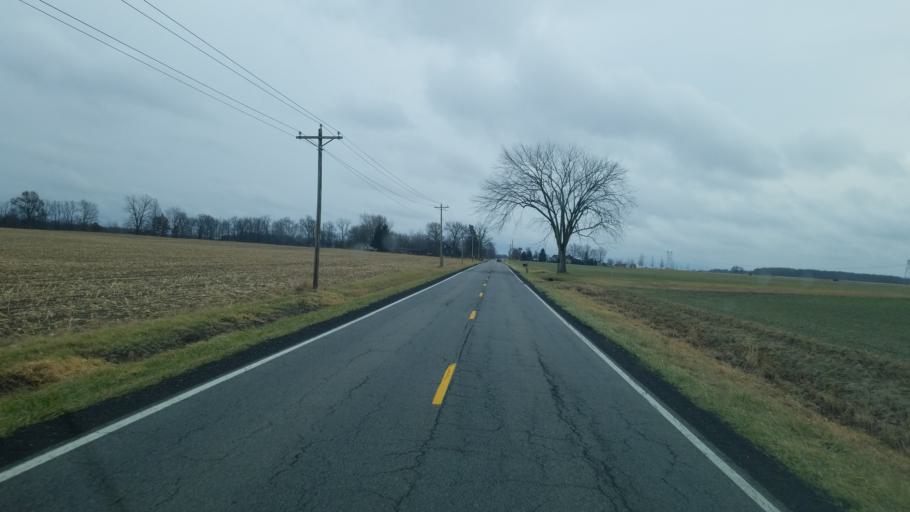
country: US
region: Ohio
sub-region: Union County
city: Marysville
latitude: 40.3141
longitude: -83.3533
